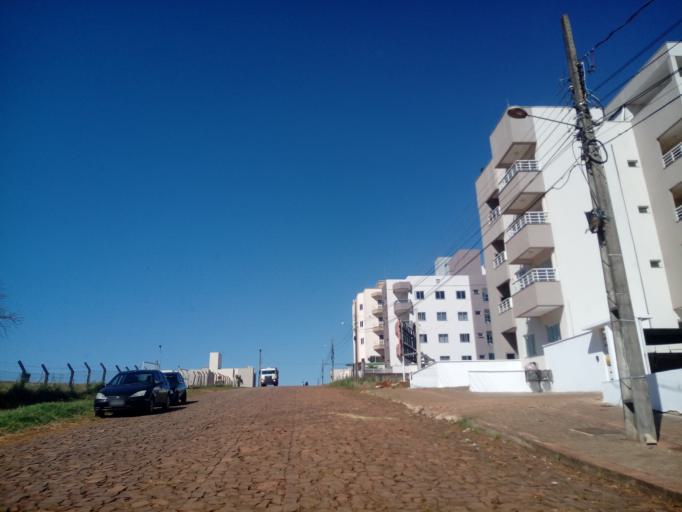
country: BR
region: Santa Catarina
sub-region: Chapeco
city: Chapeco
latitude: -27.0928
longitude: -52.6688
